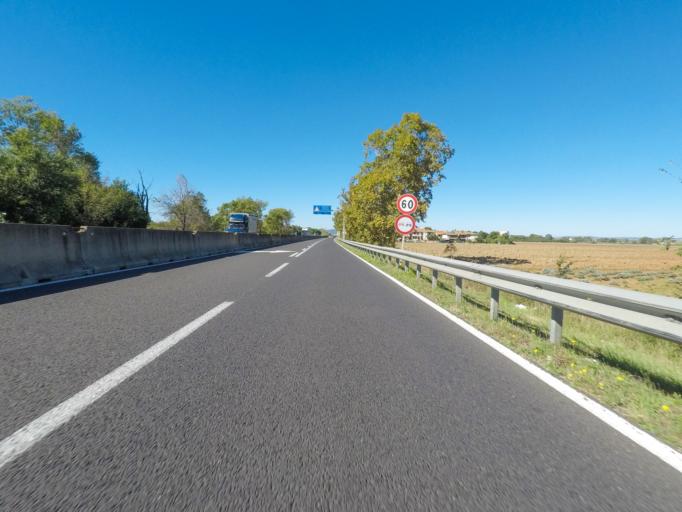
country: IT
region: Tuscany
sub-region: Provincia di Grosseto
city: Albinia
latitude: 42.4914
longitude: 11.2119
